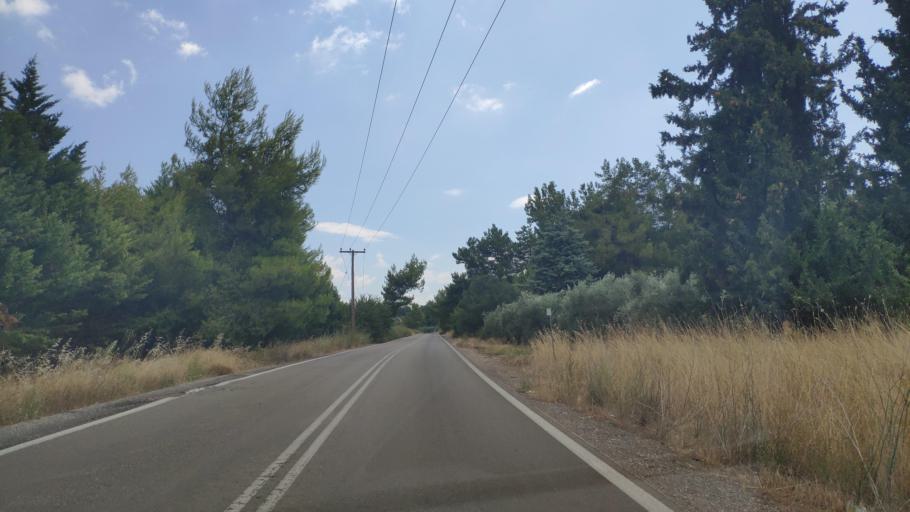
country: GR
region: Central Greece
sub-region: Nomos Fthiotidos
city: Martinon
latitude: 38.5983
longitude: 23.1787
